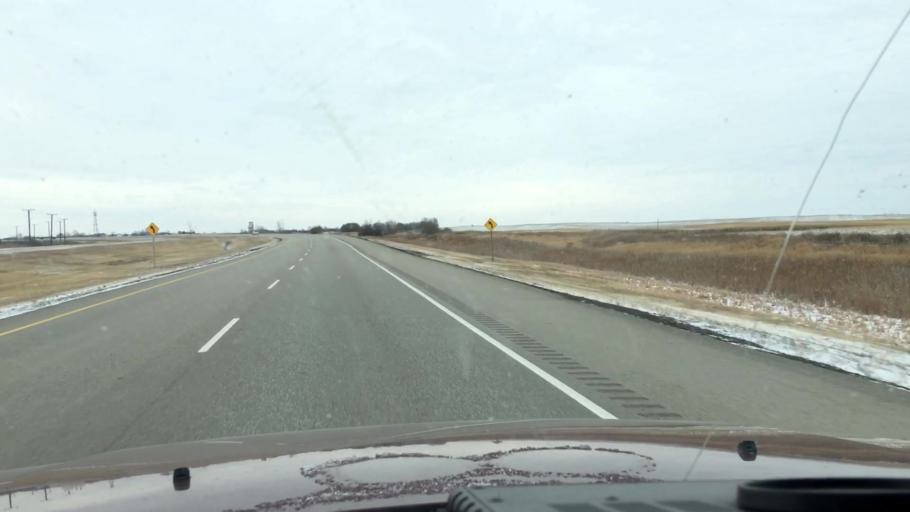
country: CA
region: Saskatchewan
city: Watrous
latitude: 51.3827
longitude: -106.1610
